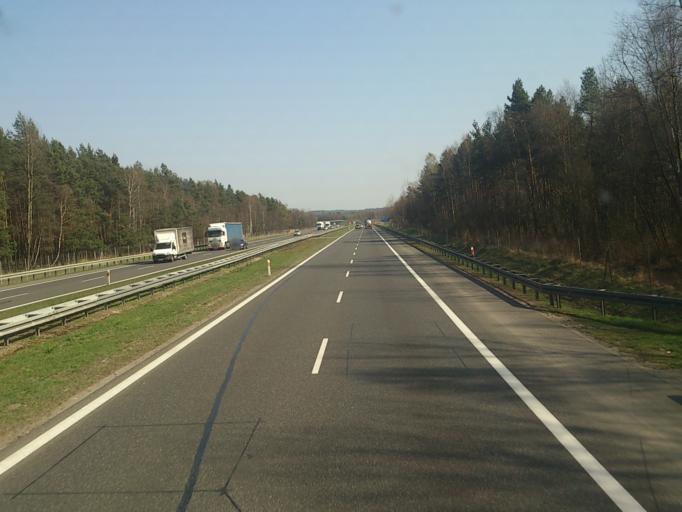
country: PL
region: Lesser Poland Voivodeship
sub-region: Powiat chrzanowski
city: Bolecin
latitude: 50.1161
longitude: 19.5015
